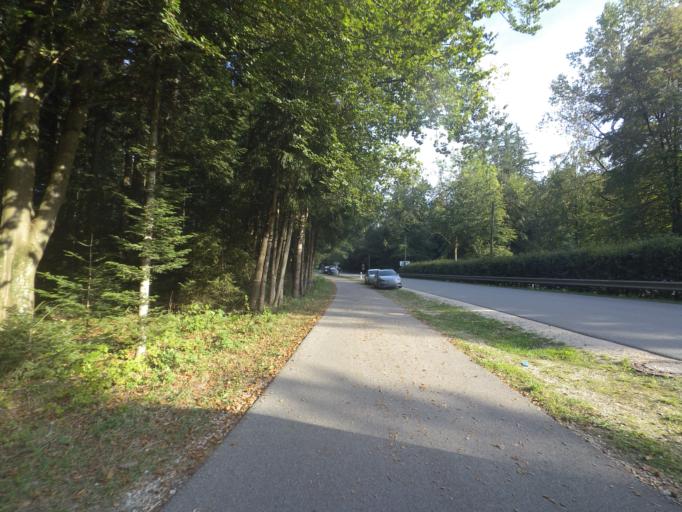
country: DE
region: Bavaria
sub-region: Upper Bavaria
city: Laufen
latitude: 47.9168
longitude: 12.9046
